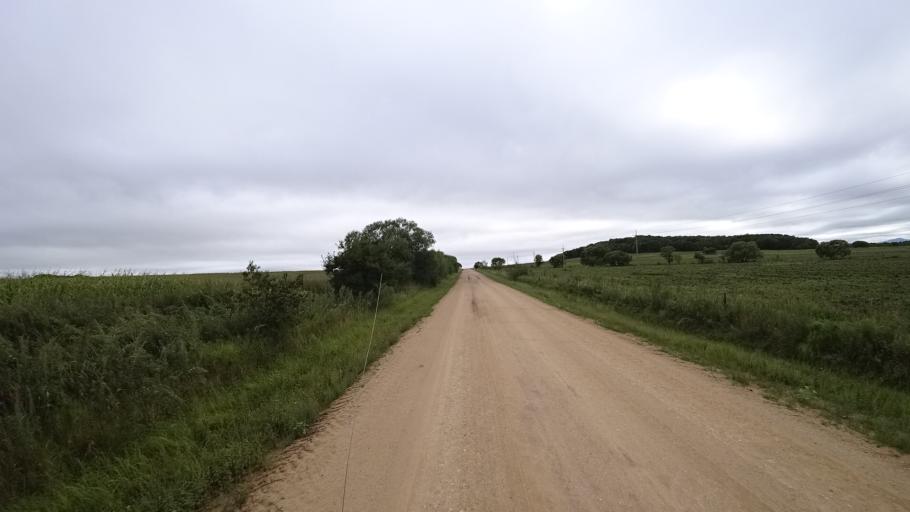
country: RU
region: Primorskiy
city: Monastyrishche
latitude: 44.0952
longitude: 132.6007
